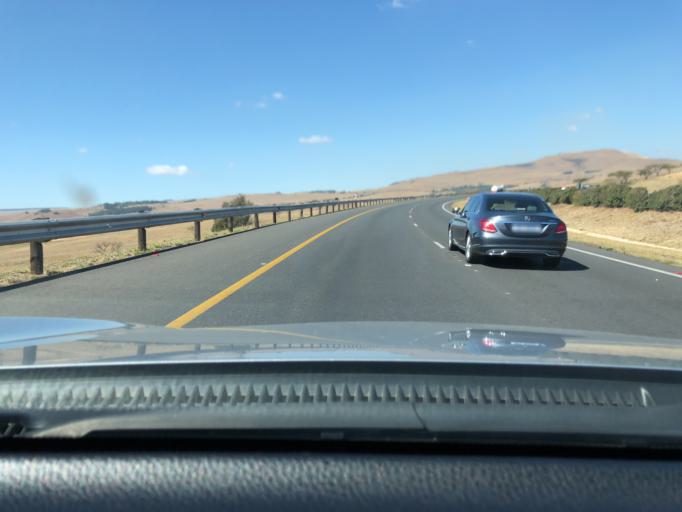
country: ZA
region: KwaZulu-Natal
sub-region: uThukela District Municipality
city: Estcourt
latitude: -29.0664
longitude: 29.9213
